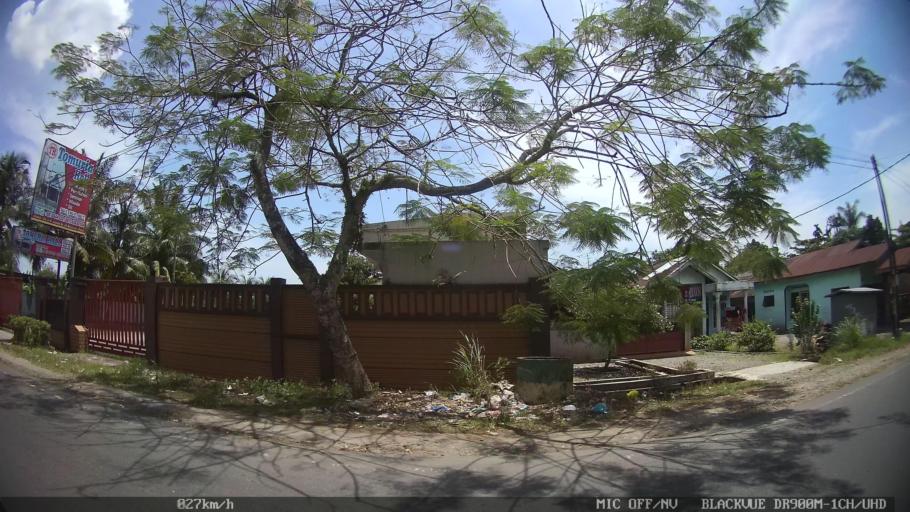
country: ID
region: North Sumatra
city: Binjai
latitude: 3.5980
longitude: 98.4993
